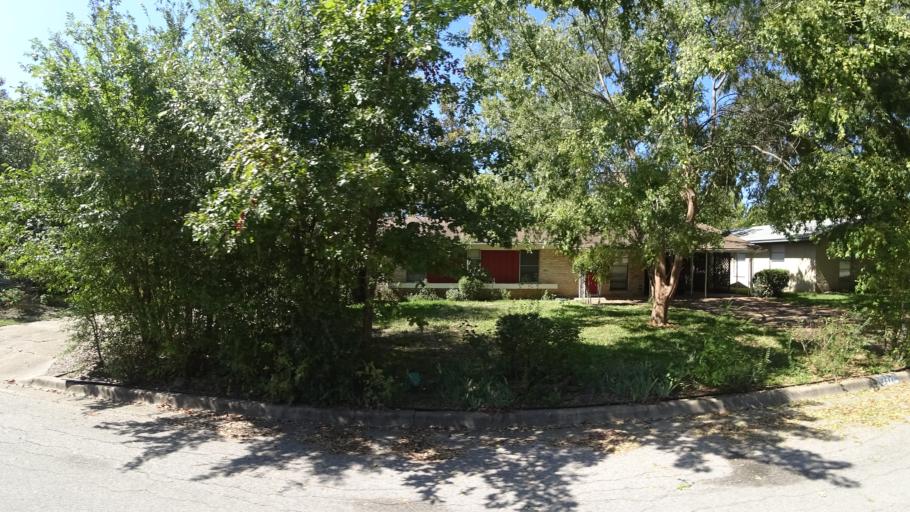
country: US
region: Texas
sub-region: Travis County
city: Austin
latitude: 30.3085
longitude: -97.6922
